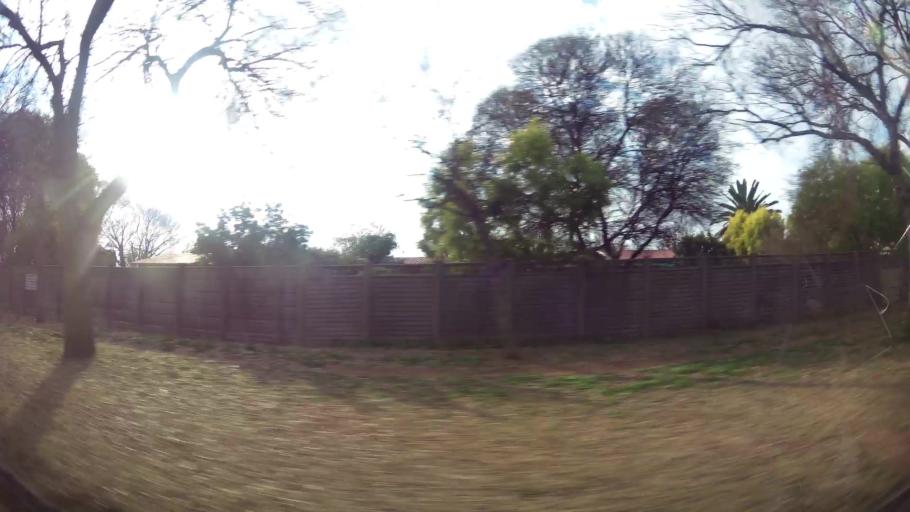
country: ZA
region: Orange Free State
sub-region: Fezile Dabi District Municipality
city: Sasolburg
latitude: -26.8181
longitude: 27.8157
